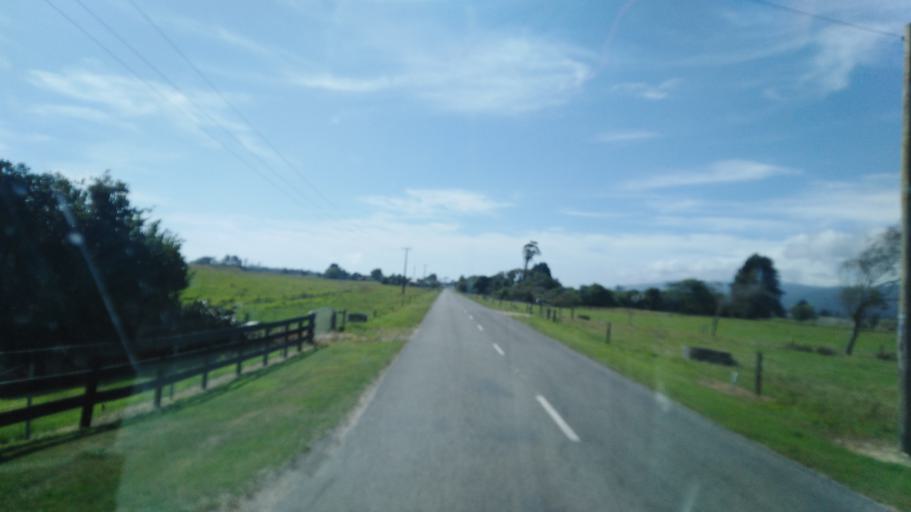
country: NZ
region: West Coast
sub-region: Buller District
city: Westport
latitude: -41.2572
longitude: 172.1313
